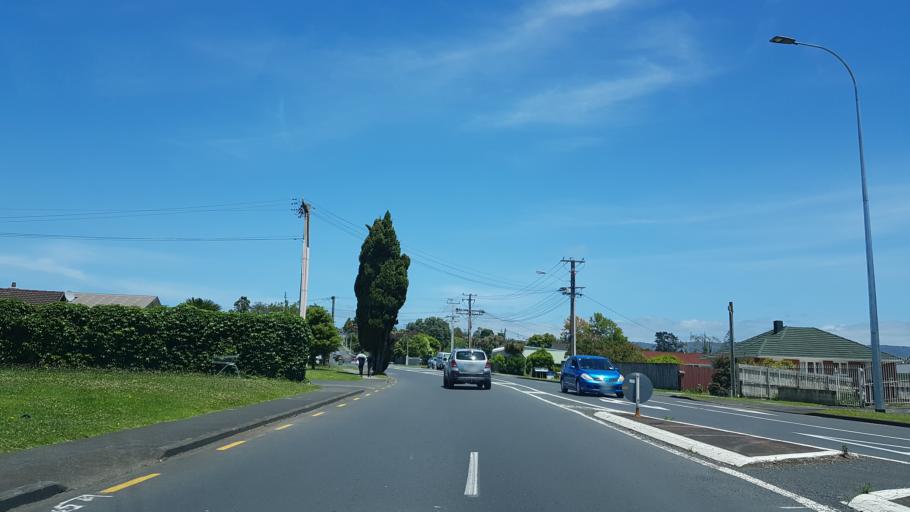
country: NZ
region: Auckland
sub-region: Auckland
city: Waitakere
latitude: -36.9096
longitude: 174.6628
